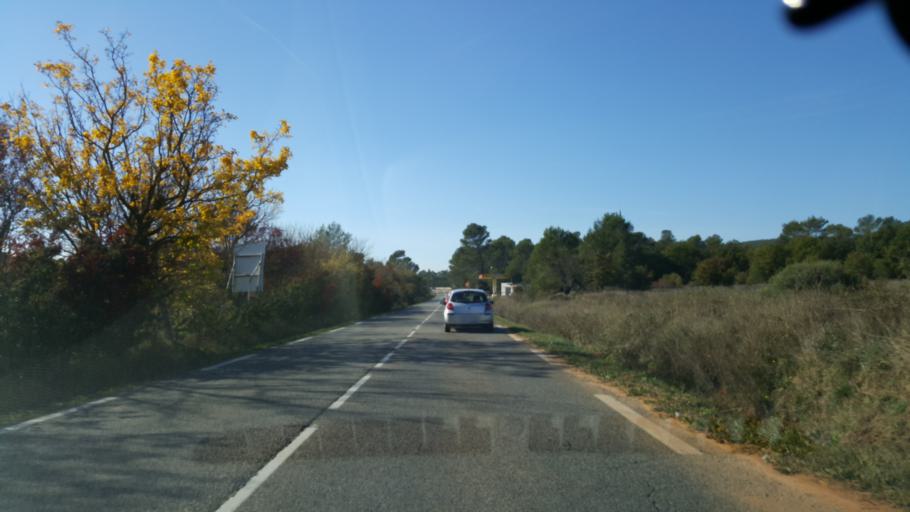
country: FR
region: Provence-Alpes-Cote d'Azur
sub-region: Departement du Var
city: Nans-les-Pins
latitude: 43.3899
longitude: 5.7676
